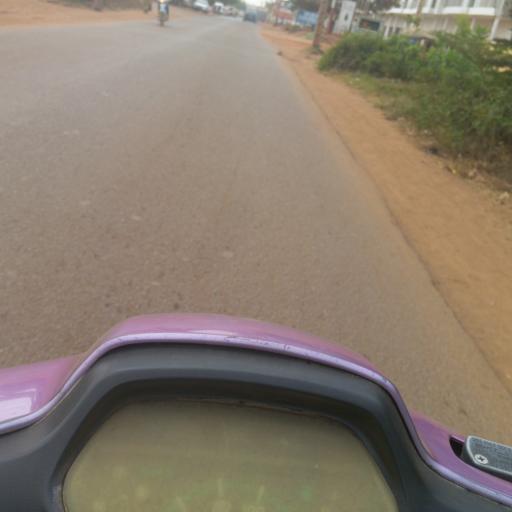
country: ML
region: Bamako
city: Bamako
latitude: 12.6569
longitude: -7.9362
